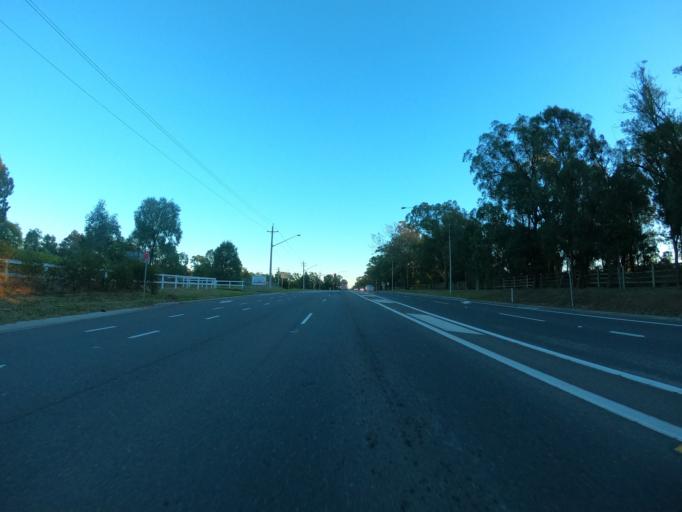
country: AU
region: New South Wales
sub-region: Hawkesbury
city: South Windsor
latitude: -33.6687
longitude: 150.8038
